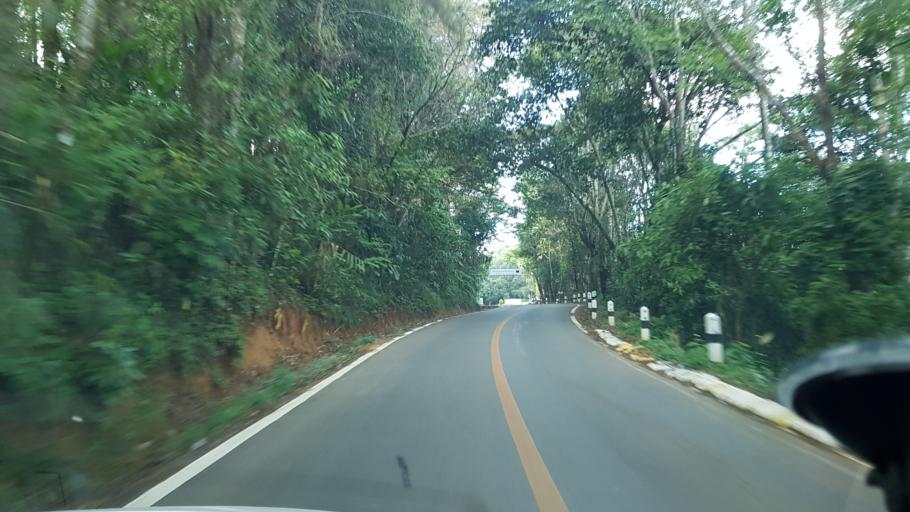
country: TH
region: Chiang Rai
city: Mae Fa Luang
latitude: 20.3325
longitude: 99.8137
